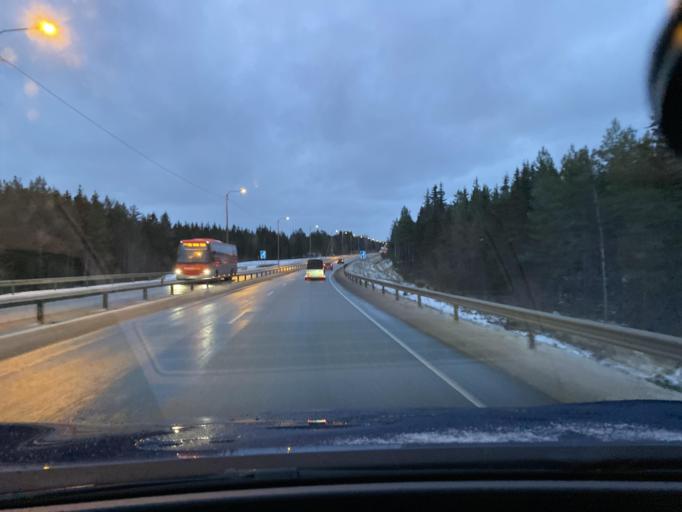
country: FI
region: Satakunta
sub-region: Rauma
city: Rauma
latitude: 61.1441
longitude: 21.5533
